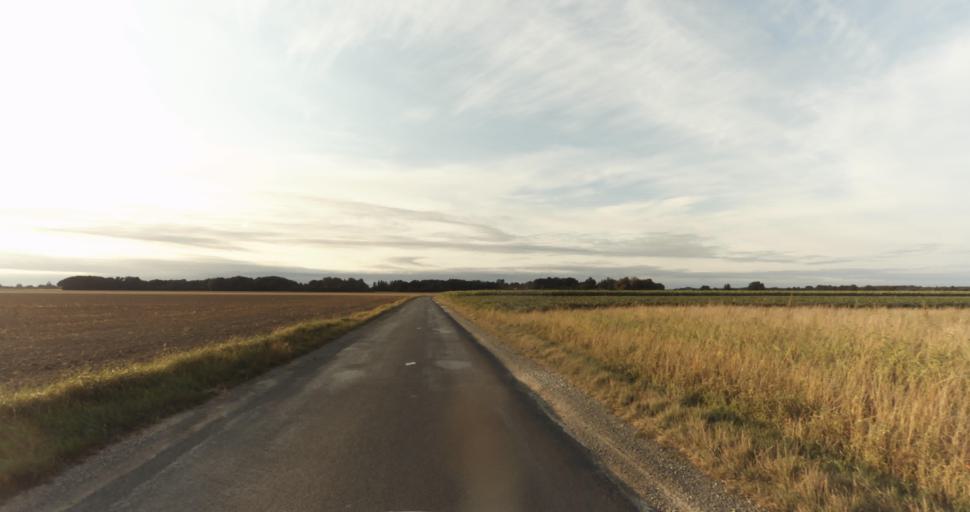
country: FR
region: Haute-Normandie
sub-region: Departement de l'Eure
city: Marcilly-sur-Eure
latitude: 48.8575
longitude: 1.2739
